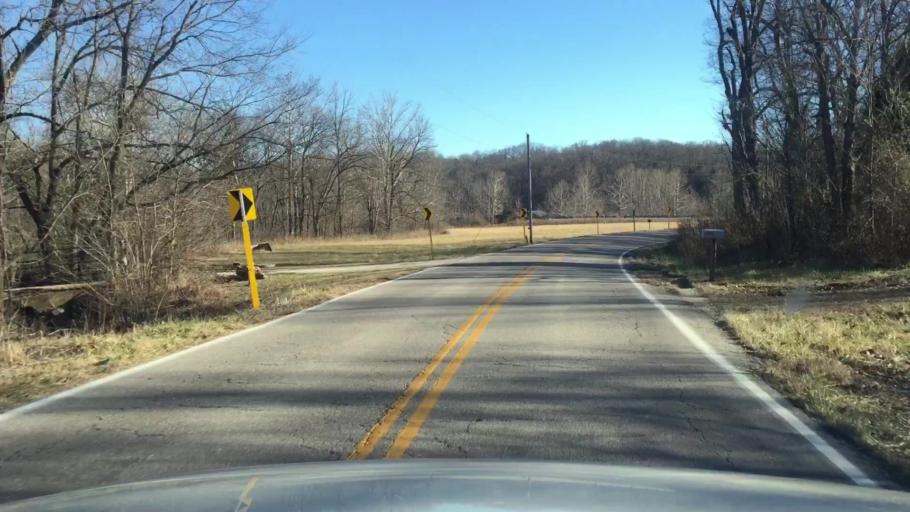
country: US
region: Missouri
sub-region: Miller County
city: Eldon
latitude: 38.3396
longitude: -92.7216
